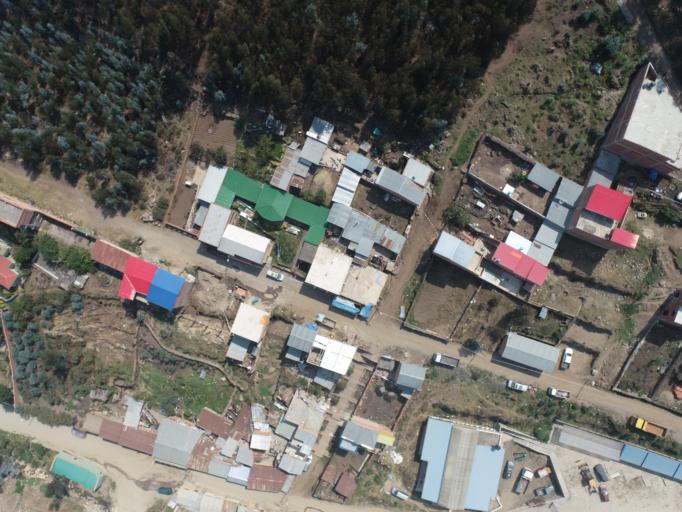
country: BO
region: La Paz
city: Quime
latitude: -16.9826
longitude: -67.2139
